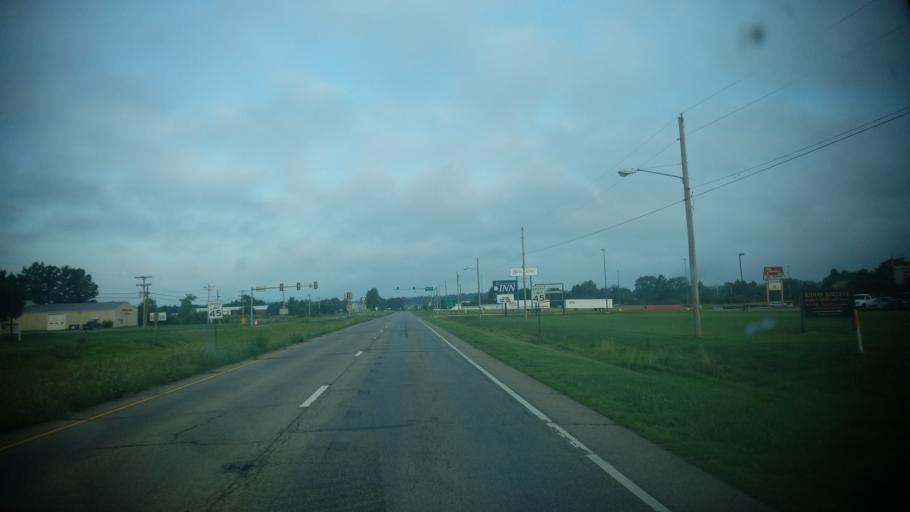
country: US
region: Illinois
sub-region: Wayne County
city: Fairfield
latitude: 38.3797
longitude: -88.3942
